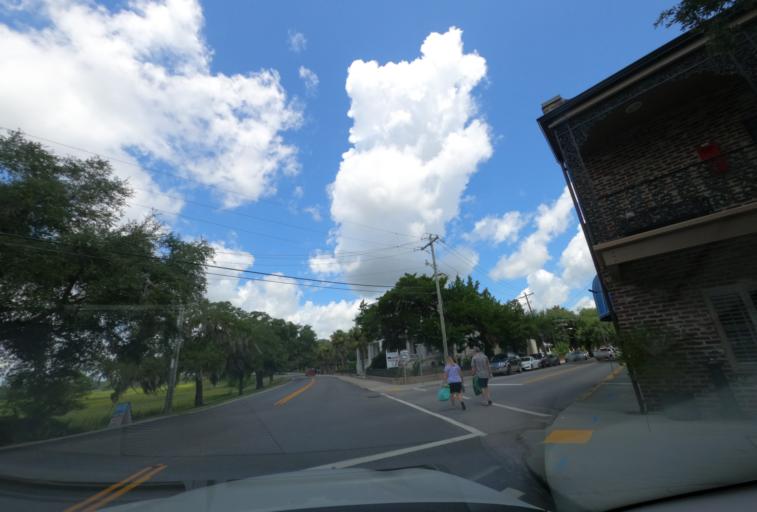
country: US
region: South Carolina
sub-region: Beaufort County
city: Beaufort
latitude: 32.4318
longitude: -80.6740
